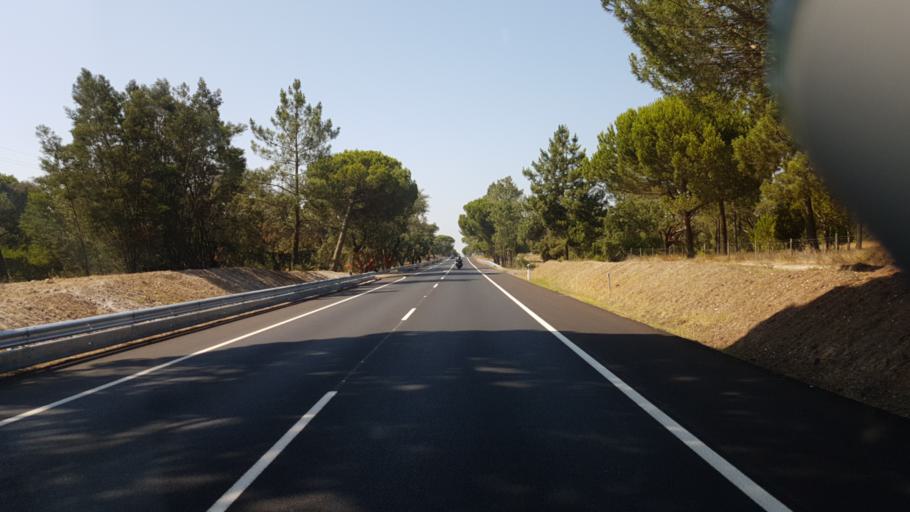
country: PT
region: Setubal
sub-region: Alcacer do Sal
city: Alcacer do Sal
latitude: 38.3030
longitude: -8.5316
